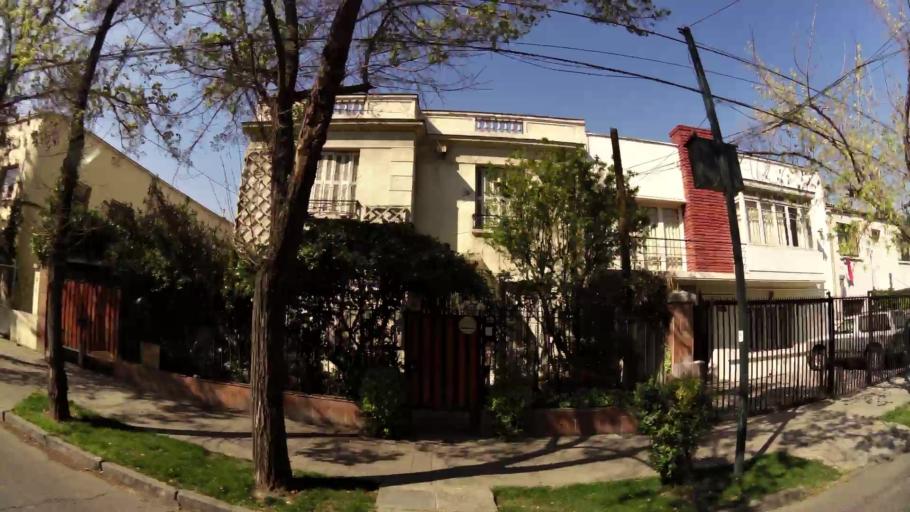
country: CL
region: Santiago Metropolitan
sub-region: Provincia de Santiago
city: Santiago
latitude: -33.4541
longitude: -70.6265
